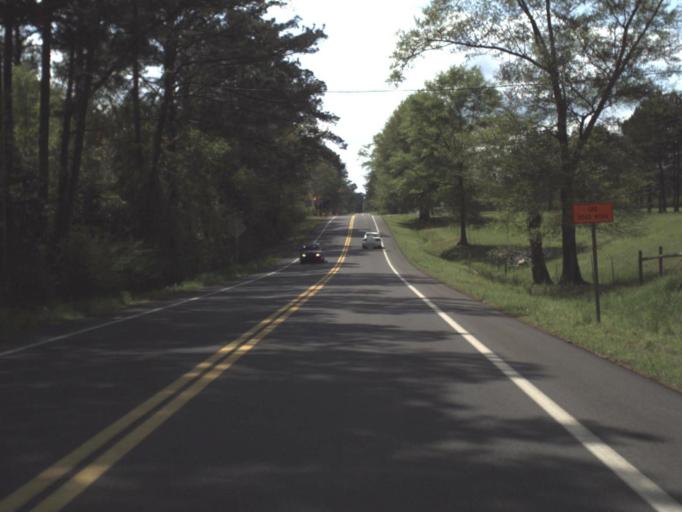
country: US
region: Alabama
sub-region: Covington County
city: Florala
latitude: 30.9666
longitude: -86.3900
